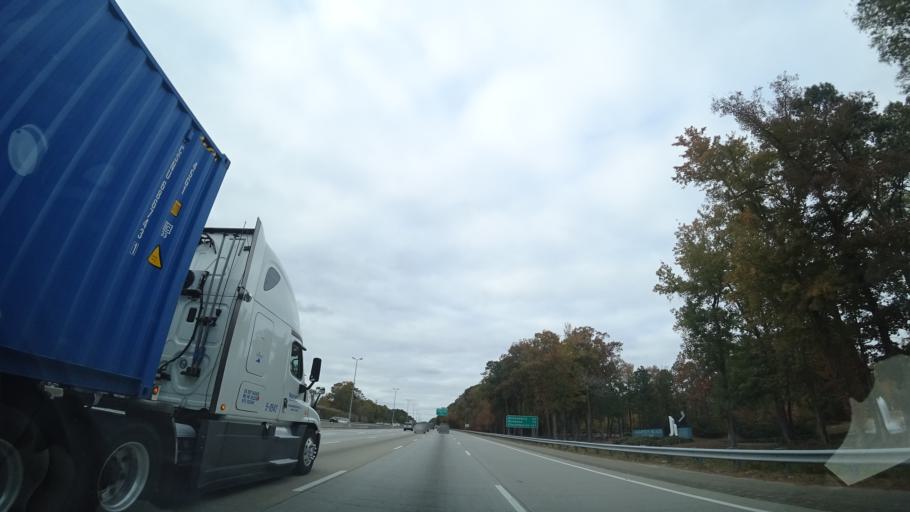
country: US
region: Virginia
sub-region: City of Hampton
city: Hampton
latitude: 37.0539
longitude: -76.4095
